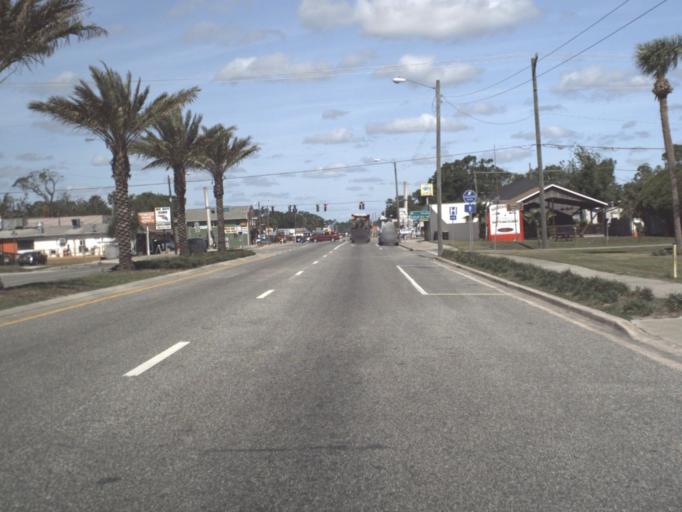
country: US
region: Florida
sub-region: Flagler County
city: Bunnell
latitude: 29.4649
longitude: -81.2562
